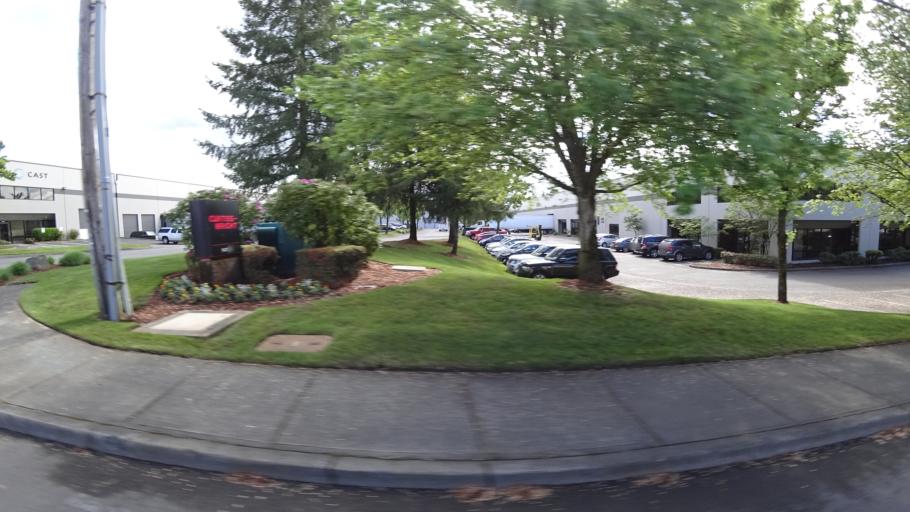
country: US
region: Oregon
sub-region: Washington County
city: Durham
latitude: 45.4179
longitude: -122.7491
